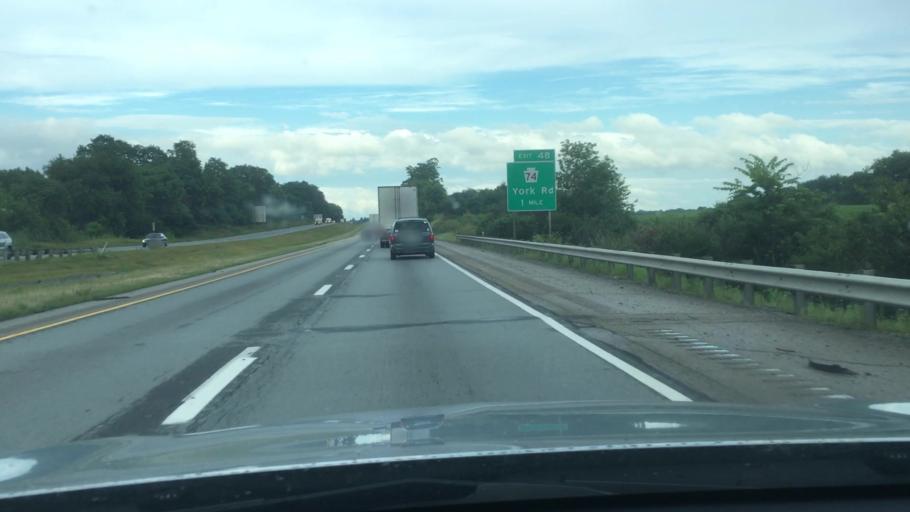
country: US
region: Pennsylvania
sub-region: Cumberland County
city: Carlisle
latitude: 40.1885
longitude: -77.1842
